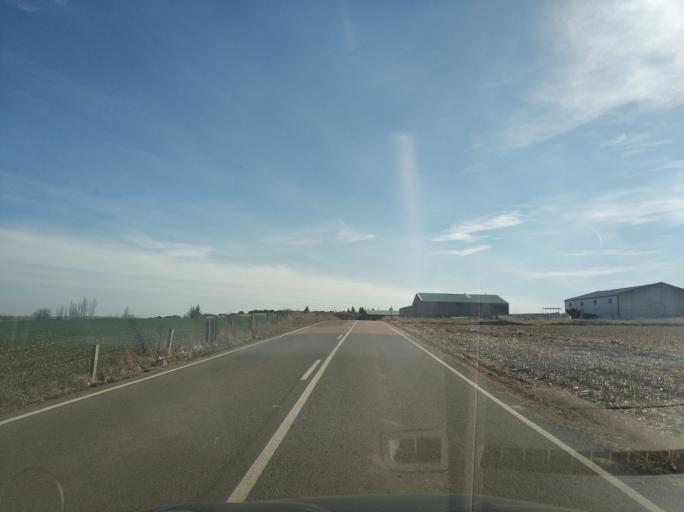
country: ES
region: Castille and Leon
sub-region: Provincia de Salamanca
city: Florida de Liebana
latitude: 41.0303
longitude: -5.7645
